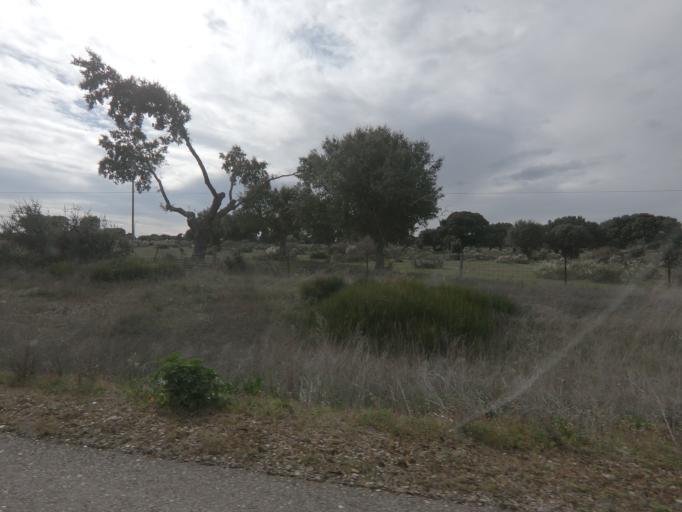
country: ES
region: Castille and Leon
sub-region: Provincia de Salamanca
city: Herguijuela de Ciudad Rodrigo
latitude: 40.4612
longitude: -6.5881
